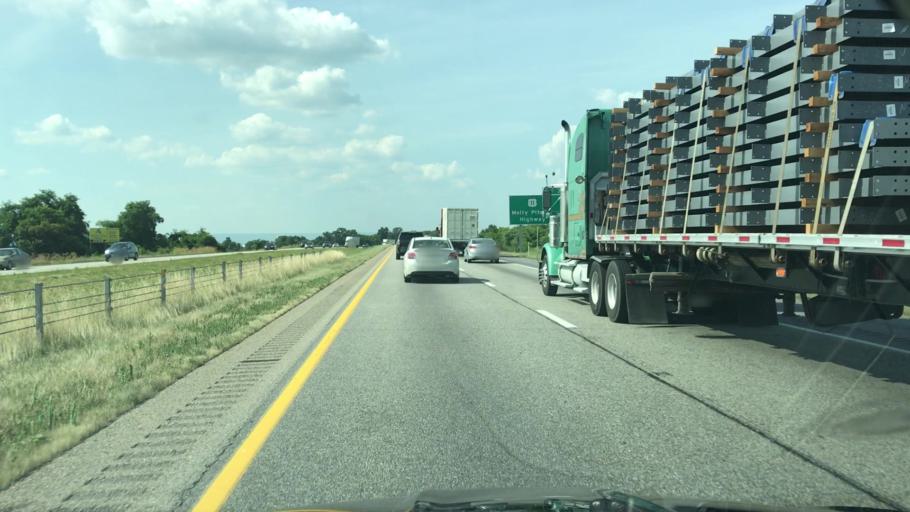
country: US
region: Pennsylvania
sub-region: Franklin County
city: State Line
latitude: 39.7477
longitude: -77.7286
